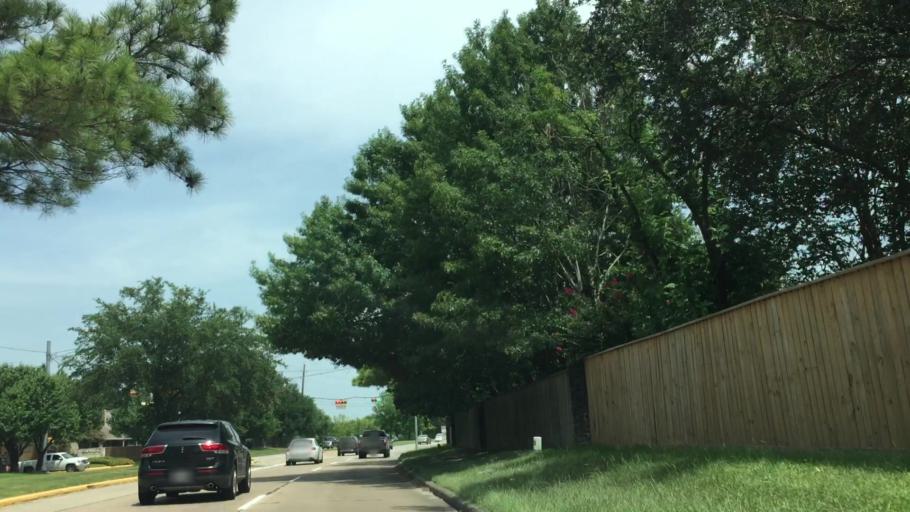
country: US
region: Texas
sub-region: Harris County
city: Jersey Village
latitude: 29.9095
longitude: -95.5659
